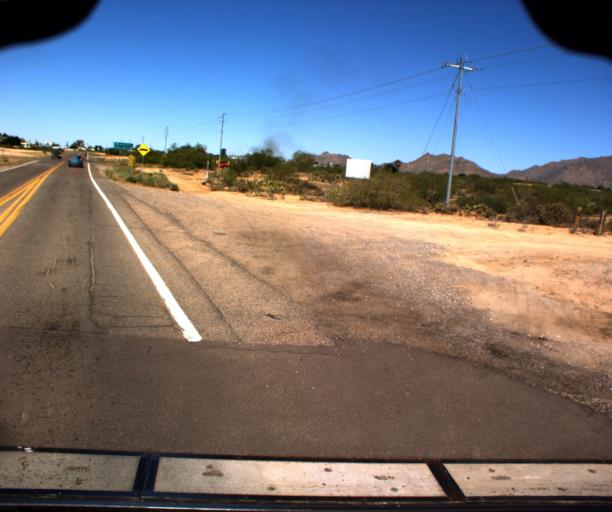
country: US
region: Arizona
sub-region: Yavapai County
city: Congress
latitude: 34.1631
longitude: -112.8458
